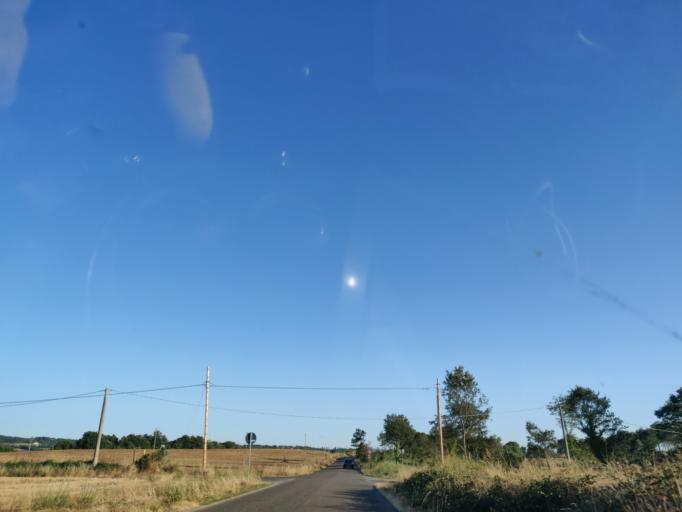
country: IT
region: Latium
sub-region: Provincia di Viterbo
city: Acquapendente
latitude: 42.7109
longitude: 11.8782
